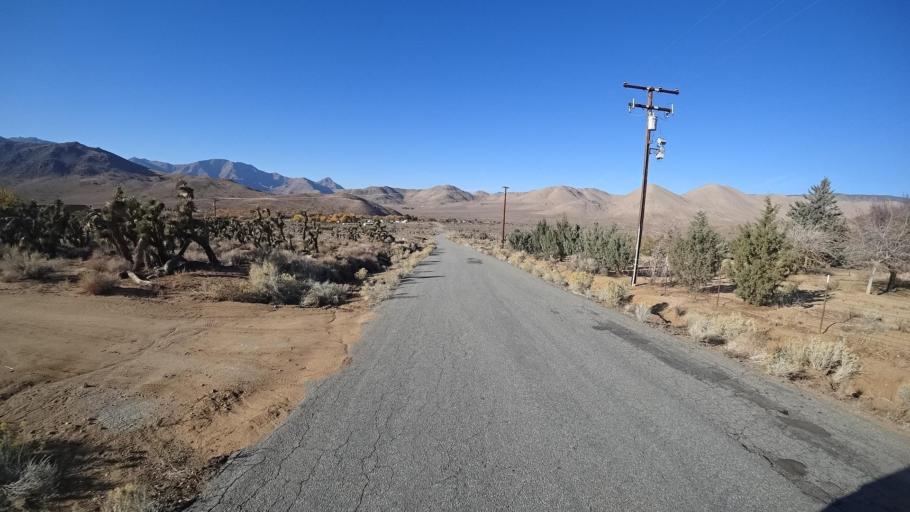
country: US
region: California
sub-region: Kern County
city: Weldon
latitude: 35.5351
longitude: -118.2025
